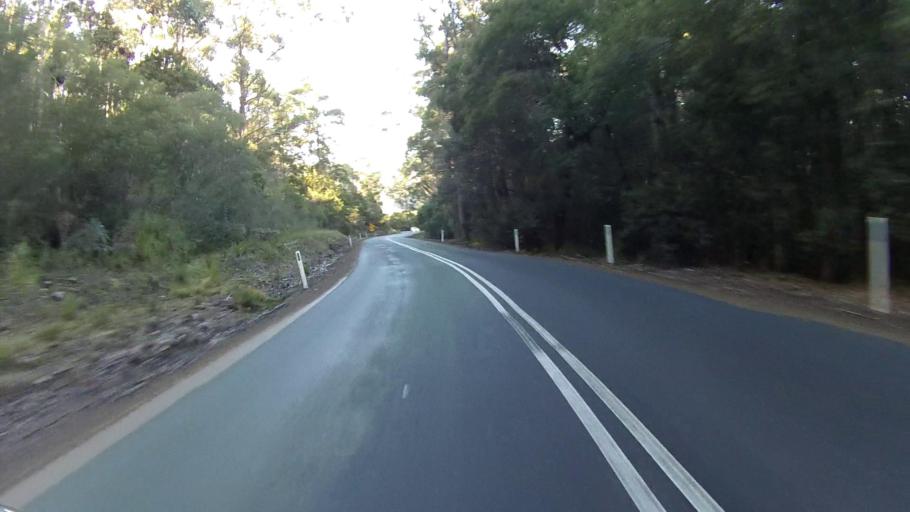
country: AU
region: Tasmania
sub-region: Clarence
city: Sandford
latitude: -43.0981
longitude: 147.8690
